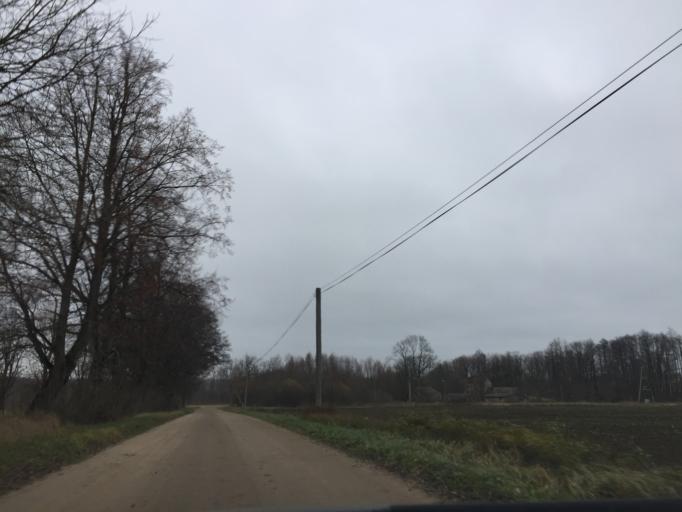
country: LV
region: Limbazu Rajons
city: Limbazi
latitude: 57.4289
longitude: 24.6602
